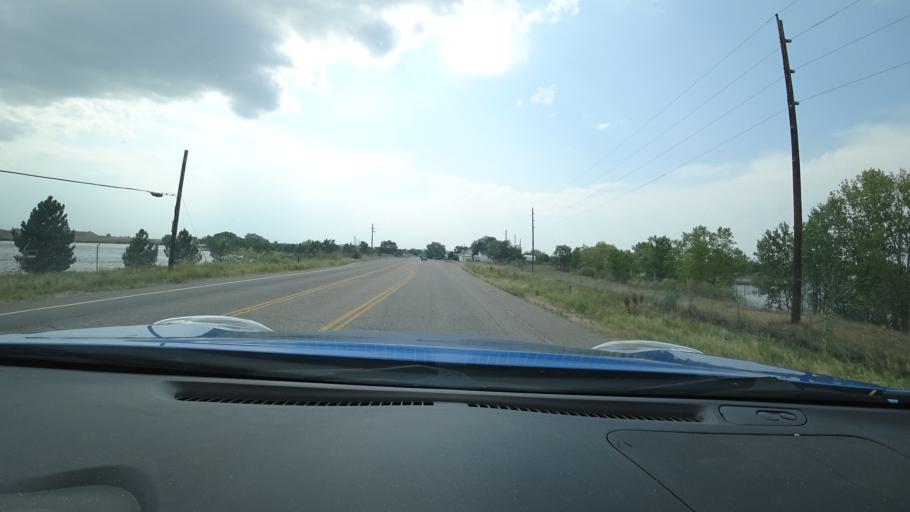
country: US
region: Colorado
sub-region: Adams County
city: Todd Creek
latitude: 39.9216
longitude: -104.8587
